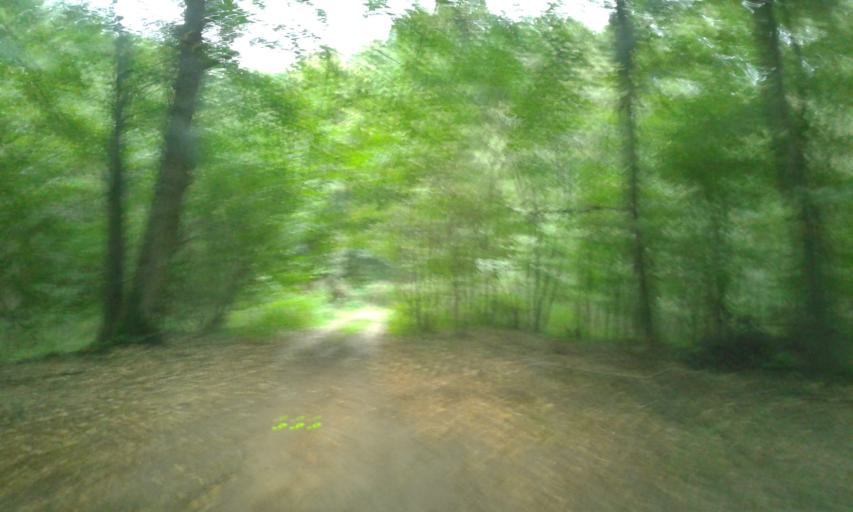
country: PL
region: West Pomeranian Voivodeship
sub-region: Powiat stargardzki
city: Dolice
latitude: 53.1867
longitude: 15.2475
